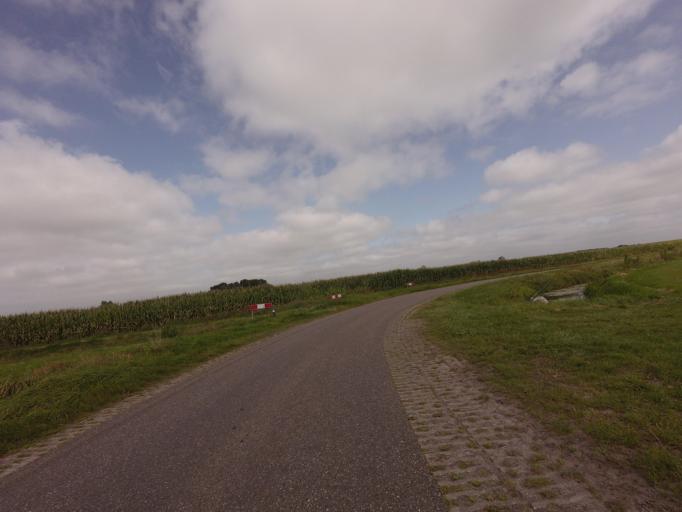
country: NL
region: Drenthe
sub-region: Gemeente Westerveld
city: Havelte
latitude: 52.8306
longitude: 6.2120
